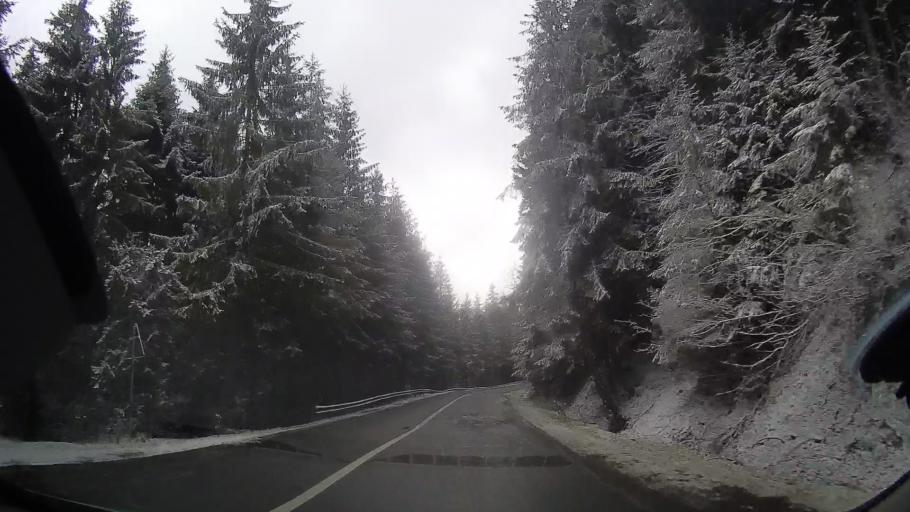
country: RO
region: Cluj
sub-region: Comuna Belis
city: Belis
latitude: 46.6589
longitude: 23.0566
